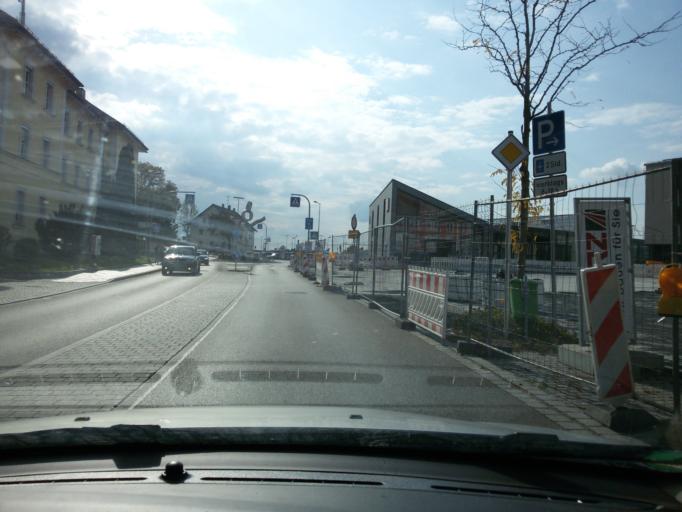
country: DE
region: Bavaria
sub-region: Swabia
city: Buchloe
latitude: 48.0340
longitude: 10.7178
